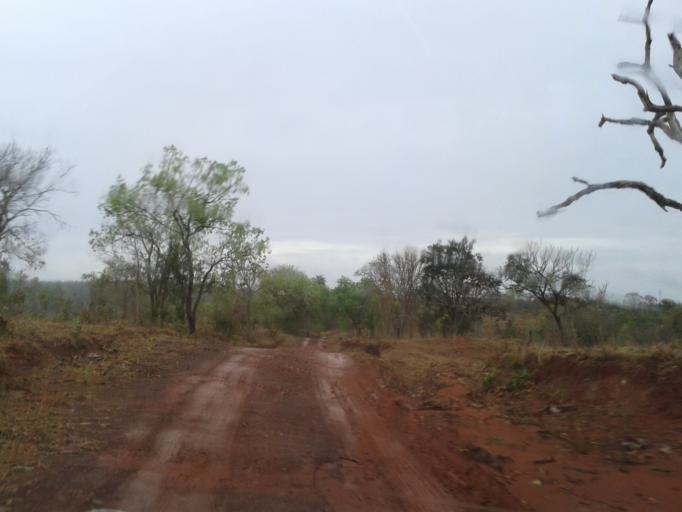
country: BR
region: Minas Gerais
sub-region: Campina Verde
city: Campina Verde
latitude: -19.3197
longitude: -49.5116
